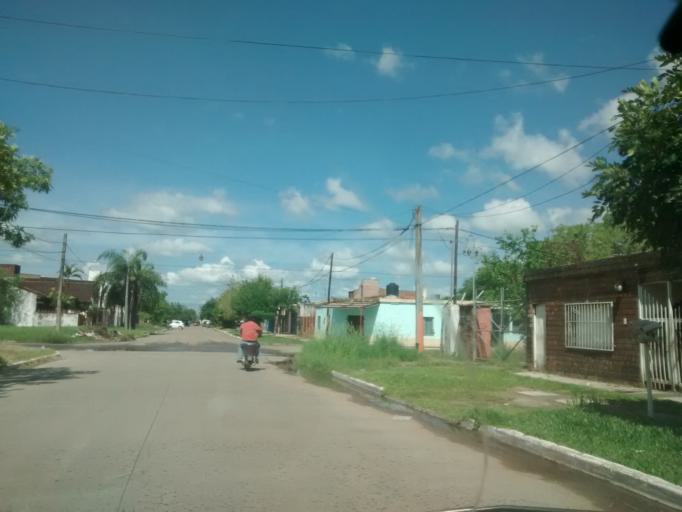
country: AR
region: Chaco
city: Resistencia
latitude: -27.4578
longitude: -59.0044
